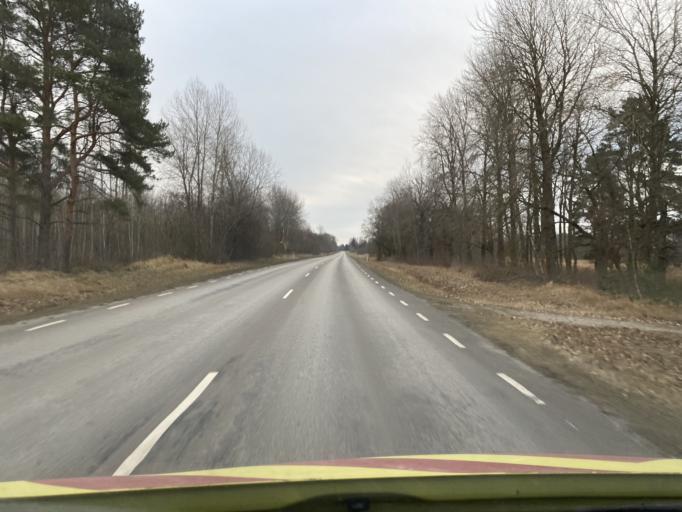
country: EE
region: Laeaene
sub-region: Ridala Parish
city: Uuemoisa
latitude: 58.8968
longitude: 23.5874
